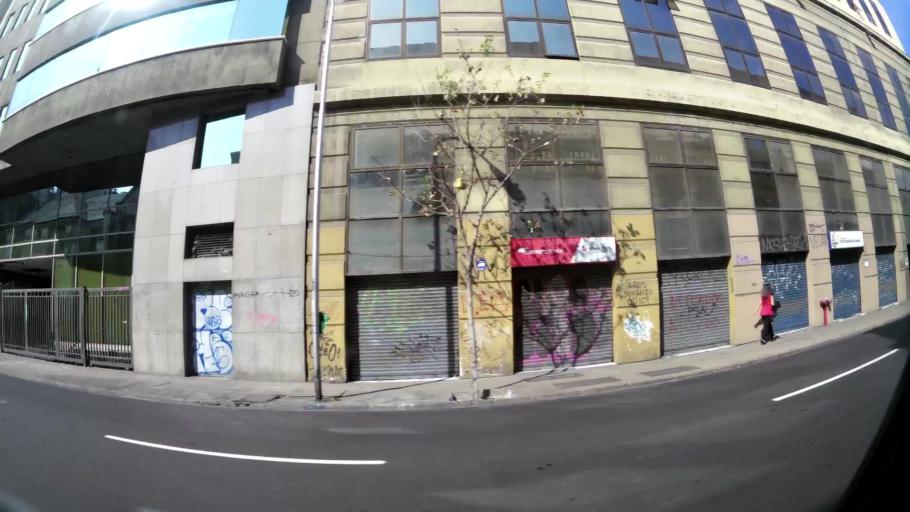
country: CL
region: Santiago Metropolitan
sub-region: Provincia de Santiago
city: Santiago
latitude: -33.4445
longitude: -70.6573
